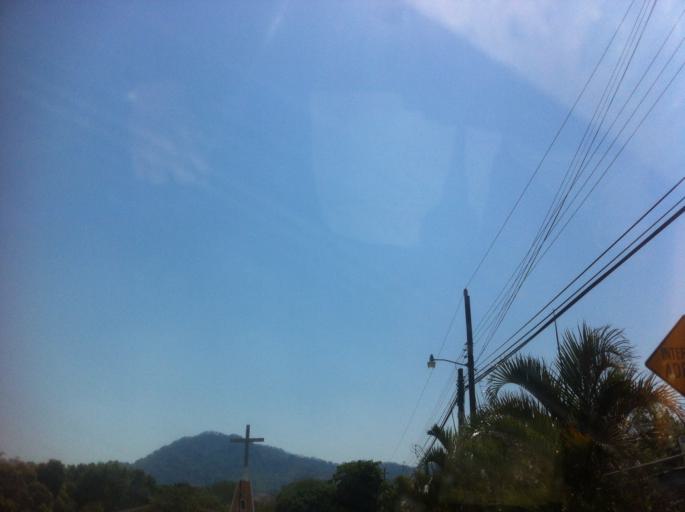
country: CR
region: Guanacaste
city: Hojancha
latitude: 10.0673
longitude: -85.4748
